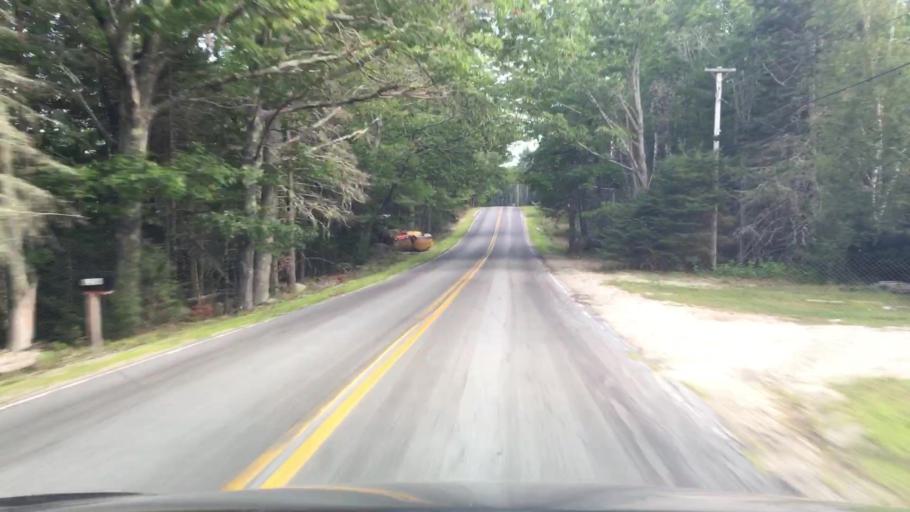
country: US
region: Maine
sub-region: Hancock County
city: Surry
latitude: 44.5114
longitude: -68.5994
